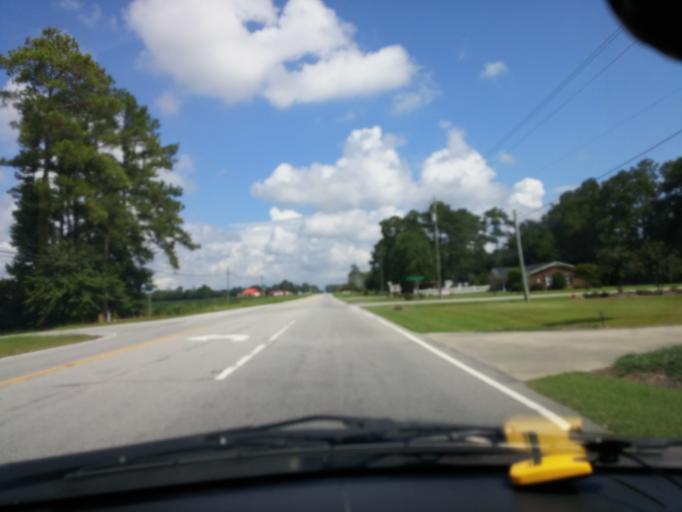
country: US
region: North Carolina
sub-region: Duplin County
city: Beulaville
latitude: 35.0682
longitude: -77.7374
